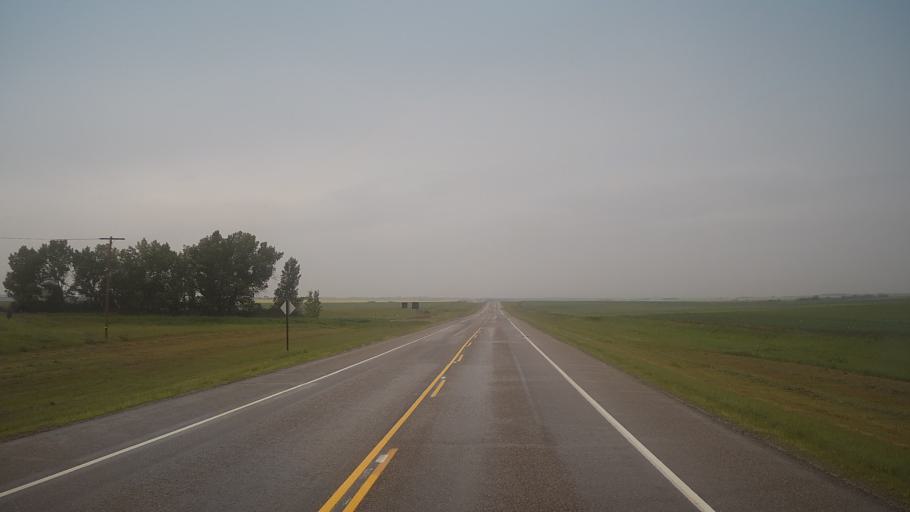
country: CA
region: Saskatchewan
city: Wilkie
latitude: 52.2047
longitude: -108.4768
